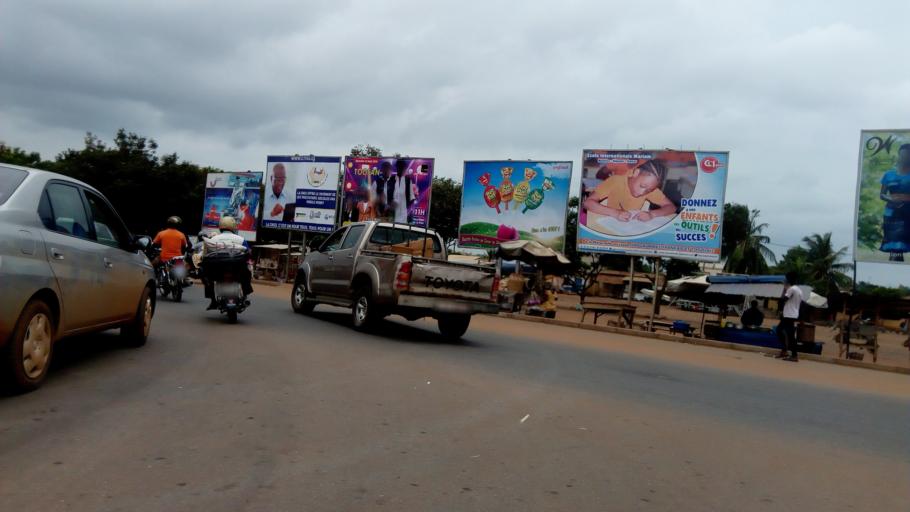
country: TG
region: Maritime
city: Lome
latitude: 6.2207
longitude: 1.2089
